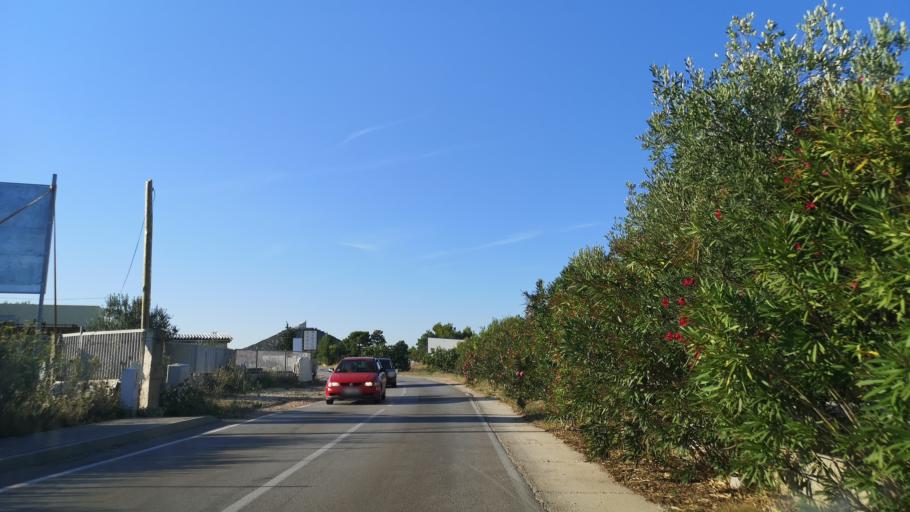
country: HR
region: Sibensko-Kniniska
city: Vodice
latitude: 43.7704
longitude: 15.7730
